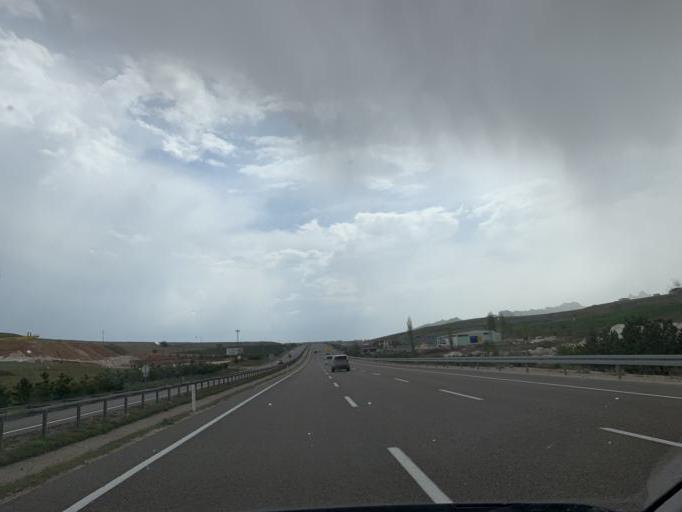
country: TR
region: Eskisehir
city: Sivrihisar
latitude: 39.4822
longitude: 31.5970
